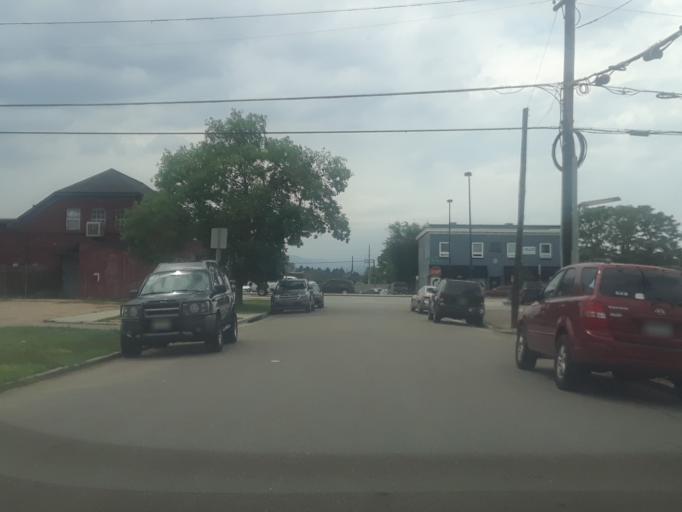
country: US
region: Colorado
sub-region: Arapahoe County
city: Englewood
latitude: 39.6894
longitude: -104.9865
